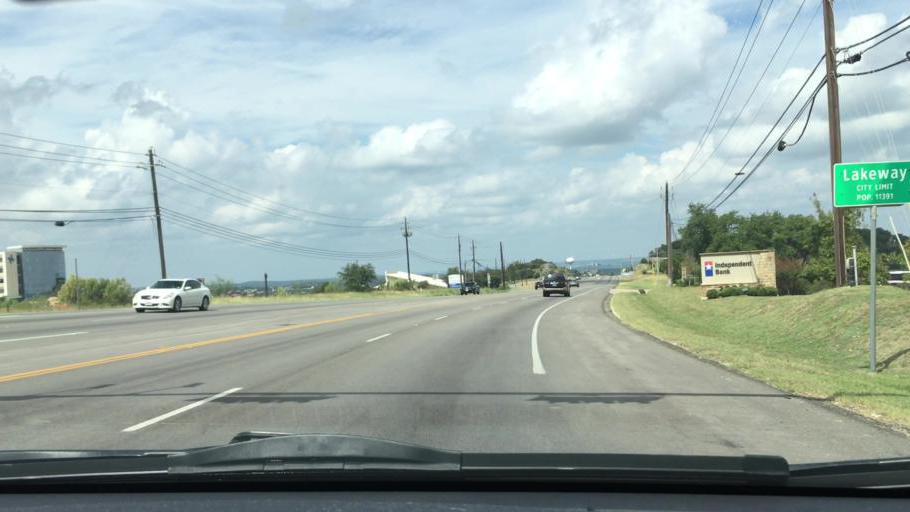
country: US
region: Texas
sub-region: Travis County
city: The Hills
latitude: 30.3308
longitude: -97.9670
